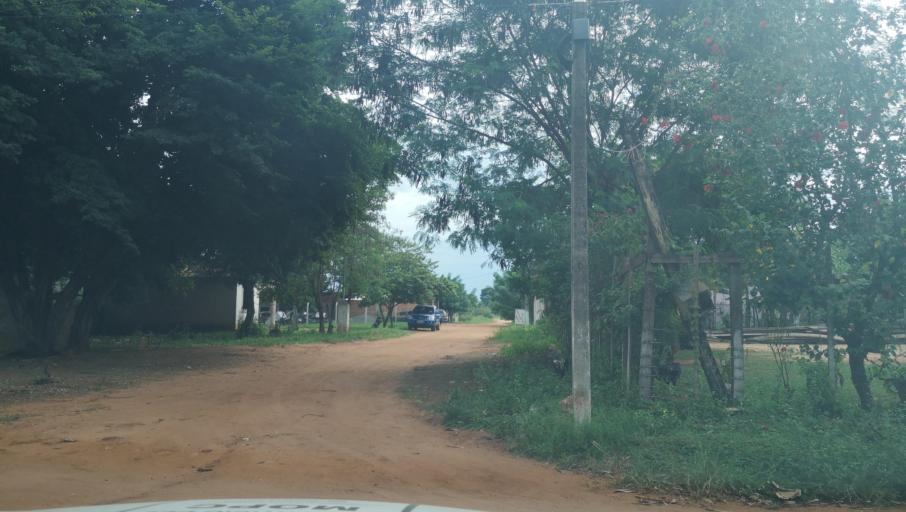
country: PY
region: San Pedro
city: Capiibary
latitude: -24.7257
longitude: -56.0216
